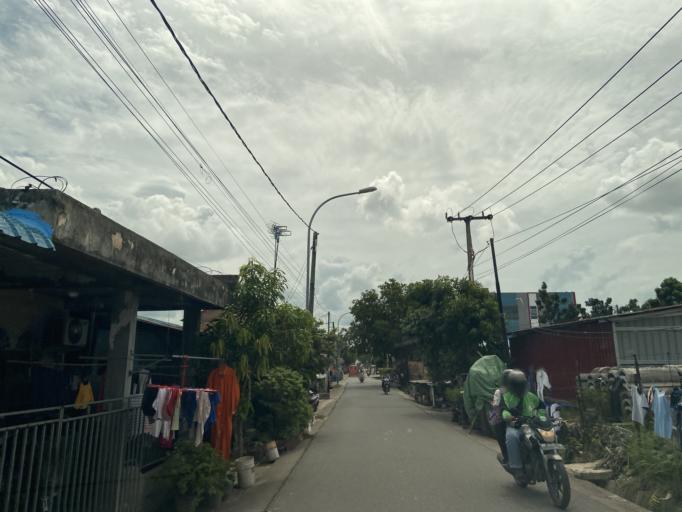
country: SG
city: Singapore
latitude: 1.0368
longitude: 103.9695
